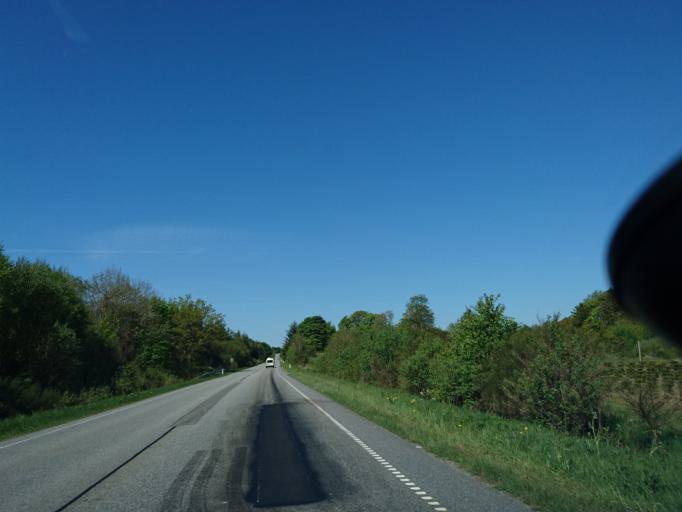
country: DK
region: North Denmark
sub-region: Hjorring Kommune
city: Sindal
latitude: 57.4578
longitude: 10.3358
